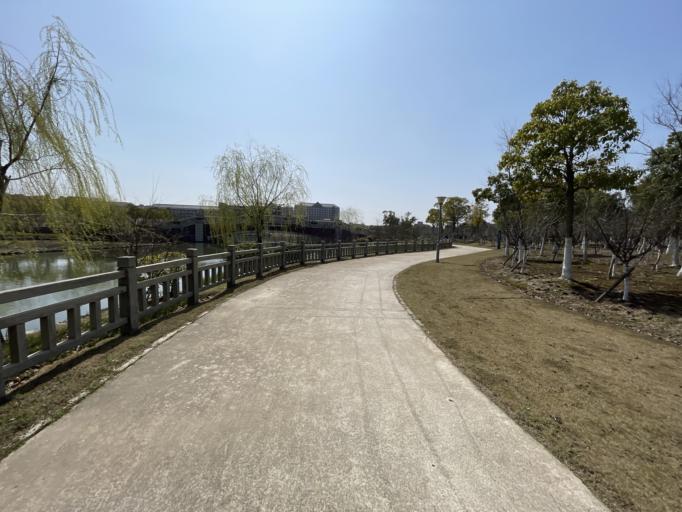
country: CN
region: Shanghai Shi
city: Shuyuan
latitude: 30.8950
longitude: 121.8860
